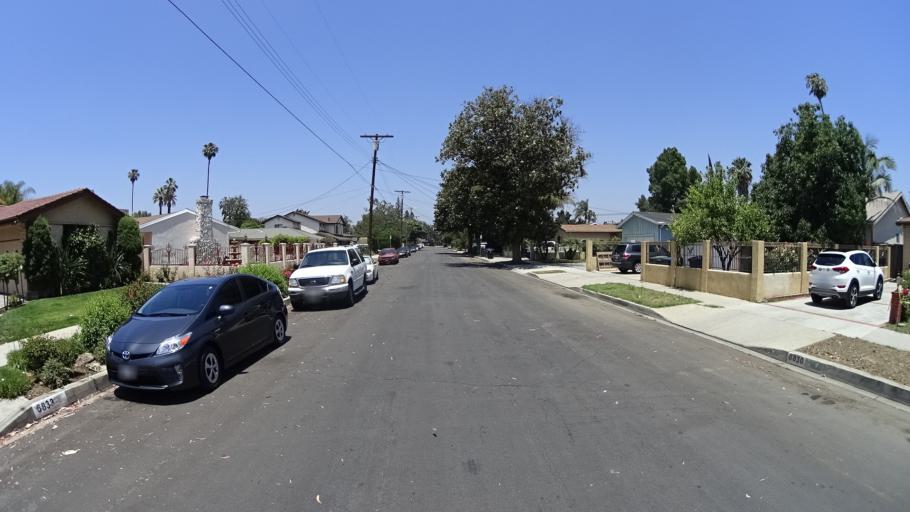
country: US
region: California
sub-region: Los Angeles County
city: Van Nuys
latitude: 34.1949
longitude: -118.4433
